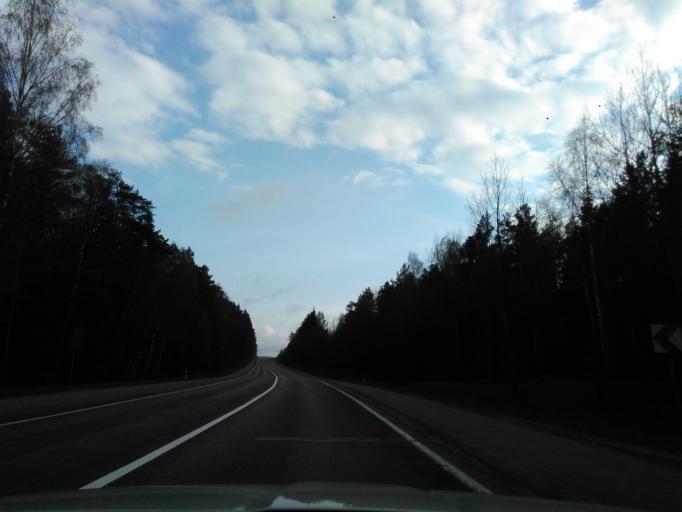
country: BY
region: Minsk
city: Lahoysk
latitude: 54.2667
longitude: 27.8569
